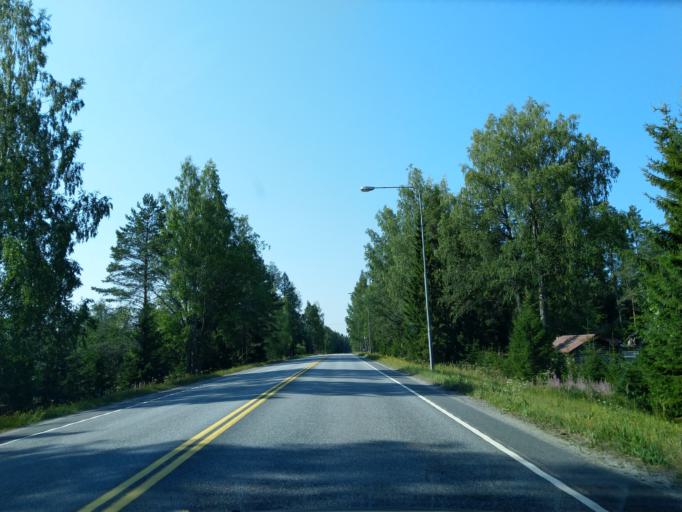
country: FI
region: Satakunta
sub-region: Pori
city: Pomarkku
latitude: 61.6625
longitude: 21.9710
